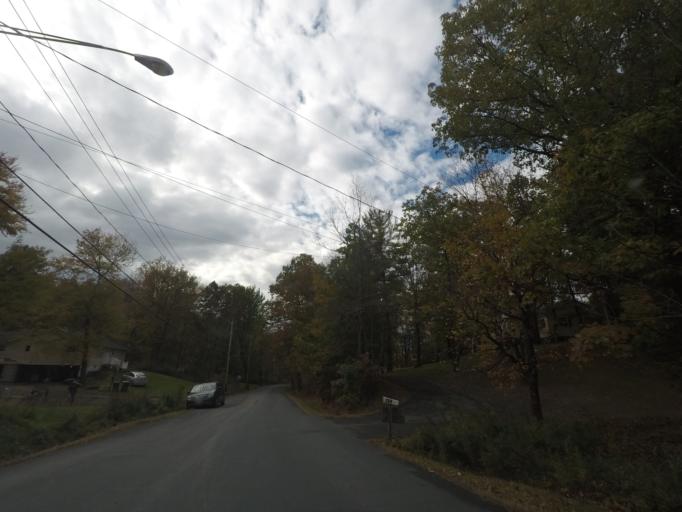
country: US
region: New York
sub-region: Rensselaer County
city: East Greenbush
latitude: 42.5813
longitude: -73.6652
